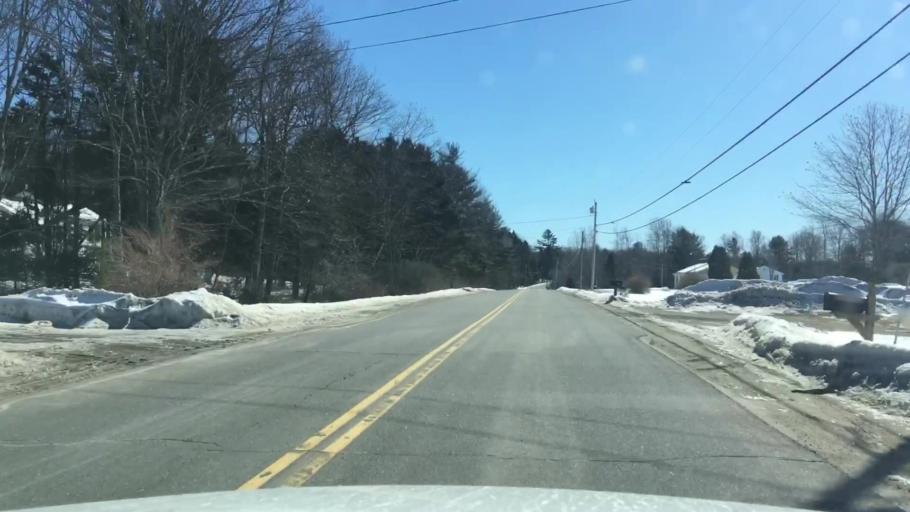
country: US
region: Maine
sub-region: Cumberland County
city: Brunswick
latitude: 43.8722
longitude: -70.0169
